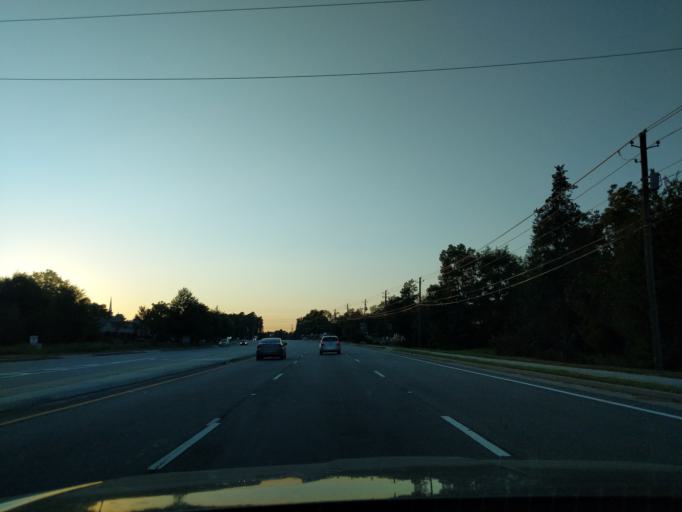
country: US
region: Georgia
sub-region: Columbia County
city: Martinez
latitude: 33.5183
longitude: -82.0780
